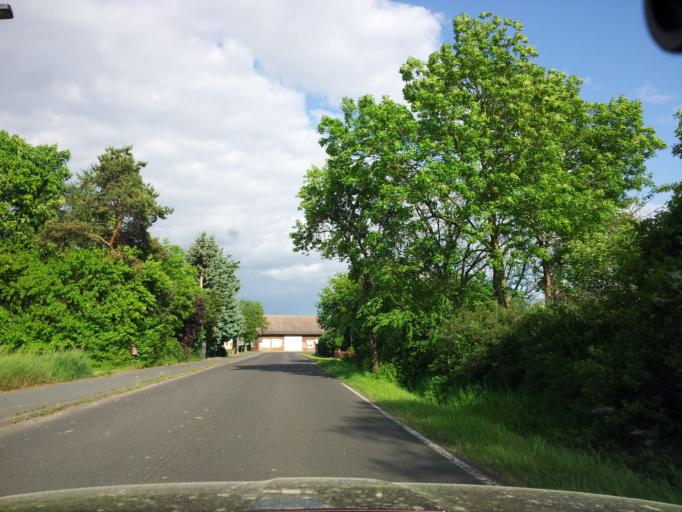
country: DE
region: Saxony-Anhalt
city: Seyda
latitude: 51.9536
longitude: 12.9066
